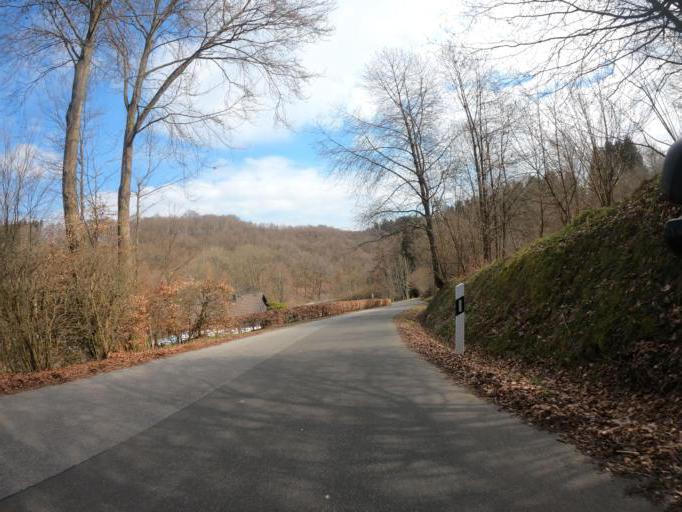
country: DE
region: North Rhine-Westphalia
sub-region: Regierungsbezirk Koln
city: Simmerath
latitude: 50.5956
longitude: 6.3108
